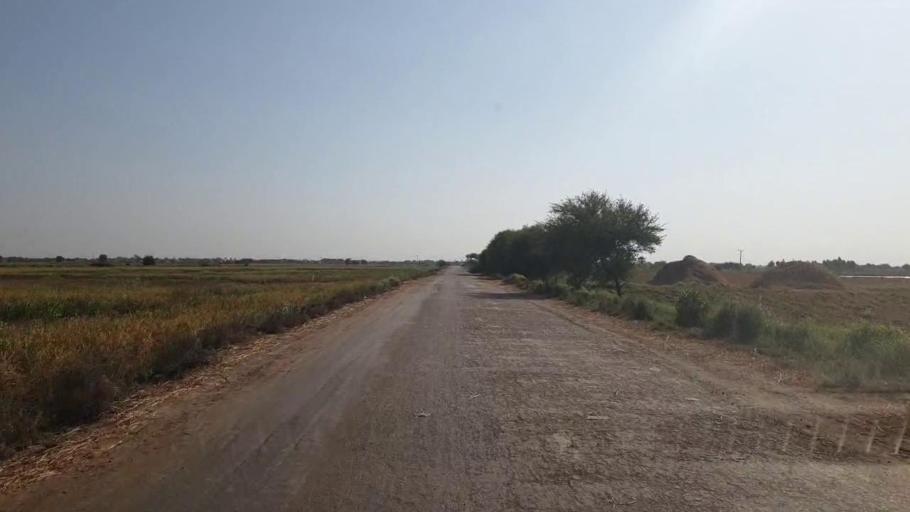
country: PK
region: Sindh
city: Matli
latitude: 25.0487
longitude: 68.7236
